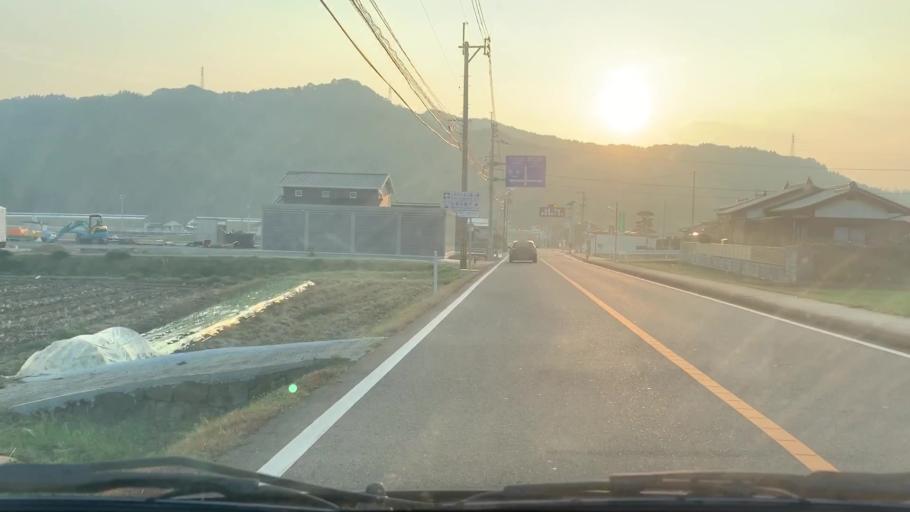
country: JP
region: Saga Prefecture
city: Takeocho-takeo
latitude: 33.2528
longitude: 129.9974
